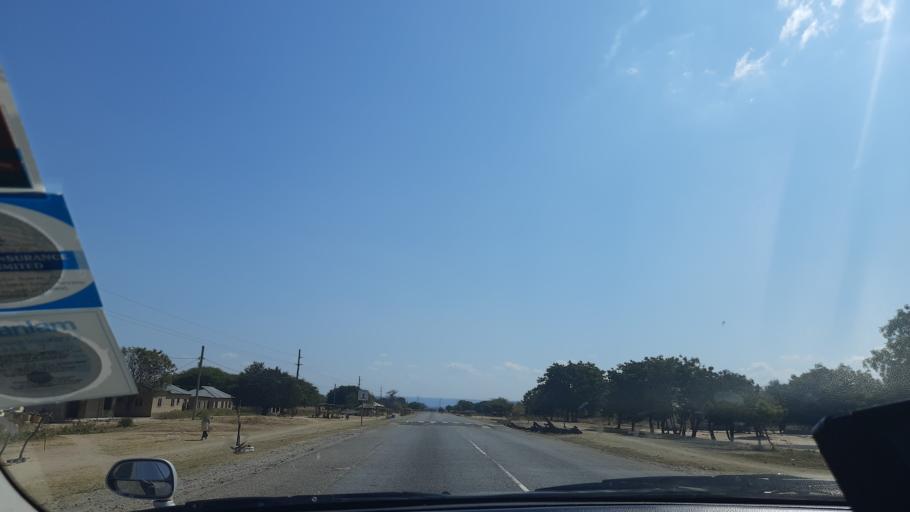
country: TZ
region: Singida
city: Kintinku
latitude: -5.8793
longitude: 35.1262
